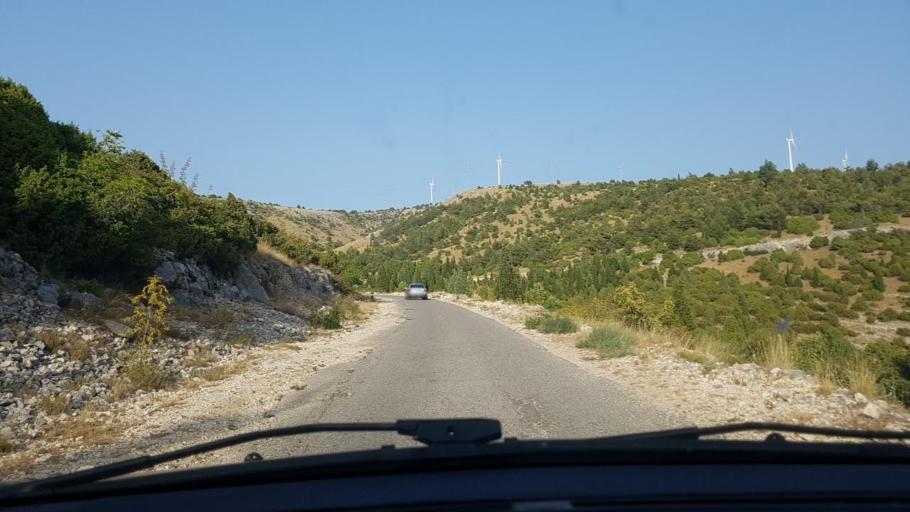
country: BA
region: Federation of Bosnia and Herzegovina
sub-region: Hercegovacko-Bosanski Kanton
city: Mostar
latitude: 43.3478
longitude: 17.8300
